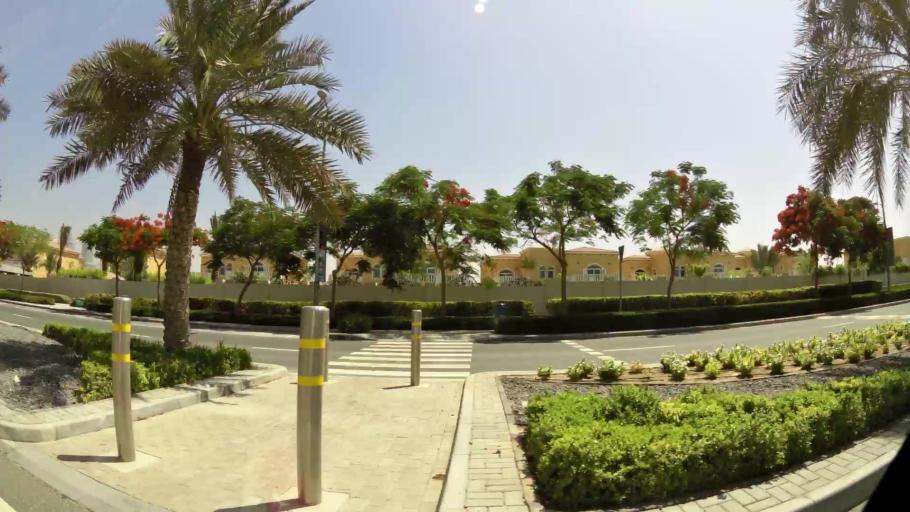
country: AE
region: Dubai
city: Dubai
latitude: 25.0538
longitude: 55.1464
